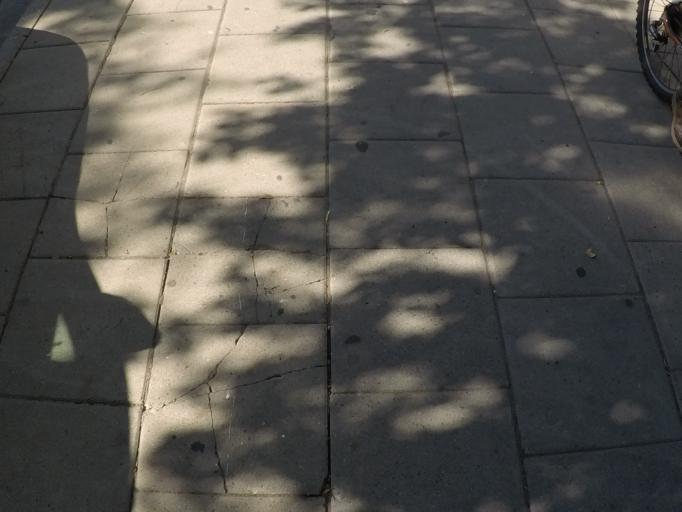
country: IL
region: Tel Aviv
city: Ramat Gan
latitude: 32.1072
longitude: 34.8011
